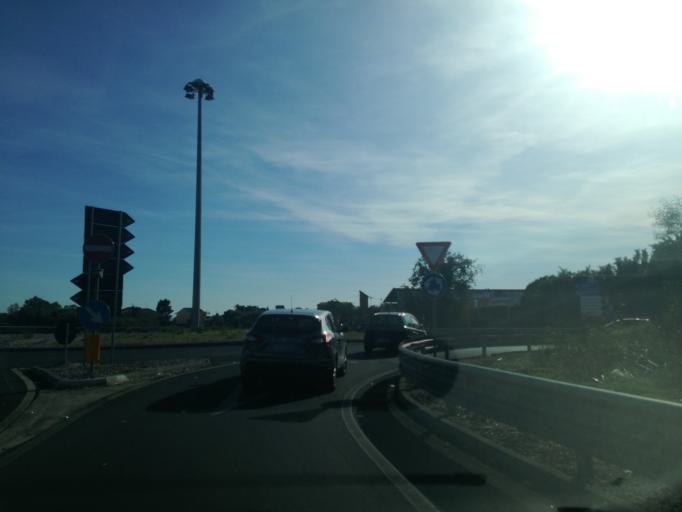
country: IT
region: Sicily
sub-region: Catania
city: Vambolieri
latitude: 37.5978
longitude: 15.1674
